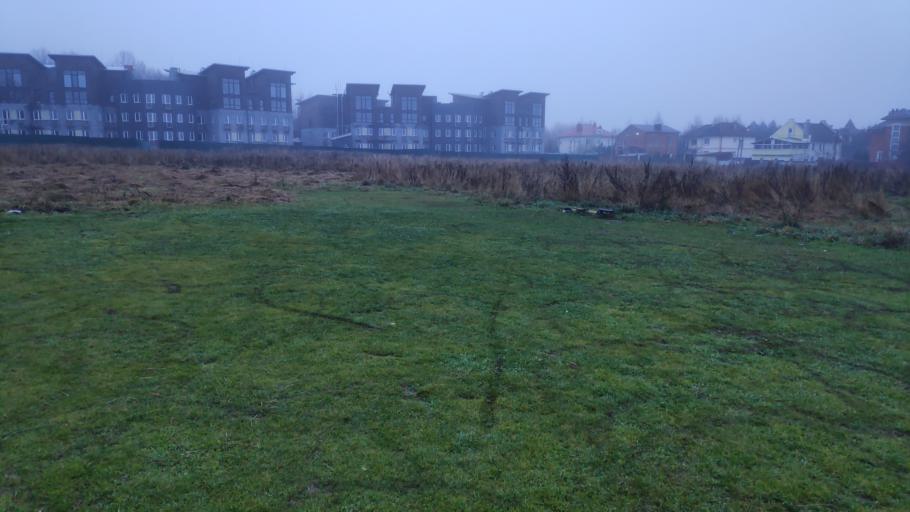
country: RU
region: Moscow
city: Gol'yanovo
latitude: 55.8352
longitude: 37.8295
